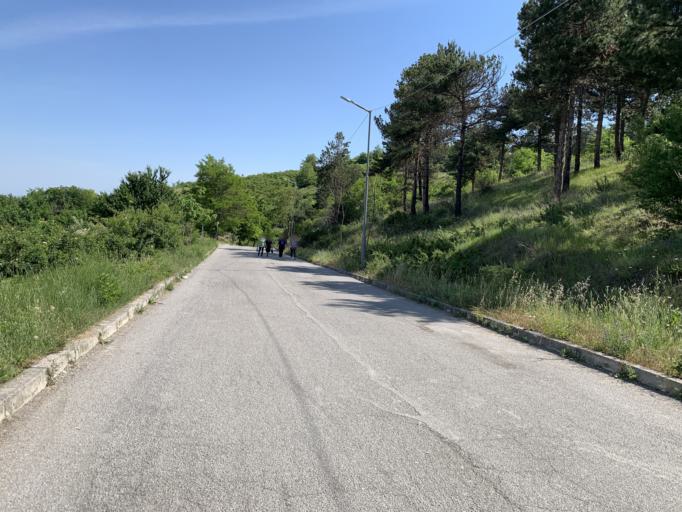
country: AL
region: Korce
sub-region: Rrethi i Korces
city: Korce
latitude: 40.6163
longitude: 20.7876
